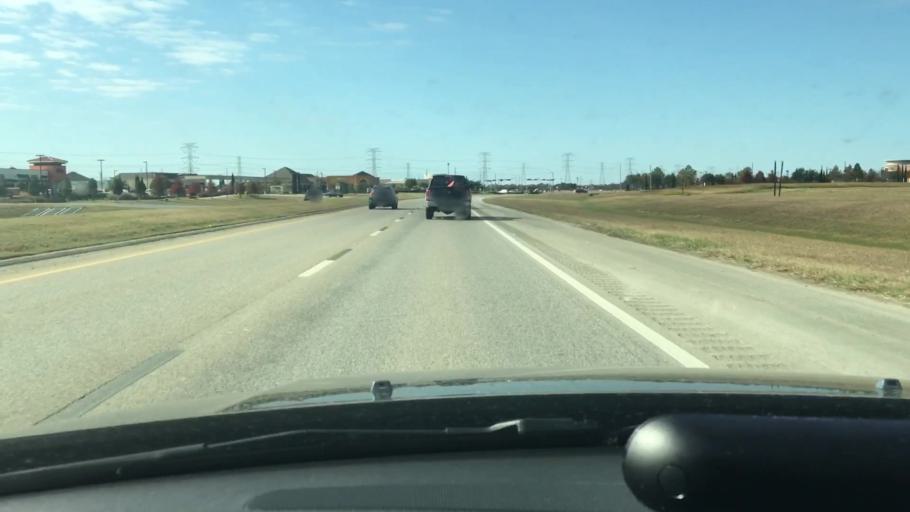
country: US
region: Texas
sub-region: Galveston County
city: Dickinson
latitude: 29.4966
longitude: -95.0596
